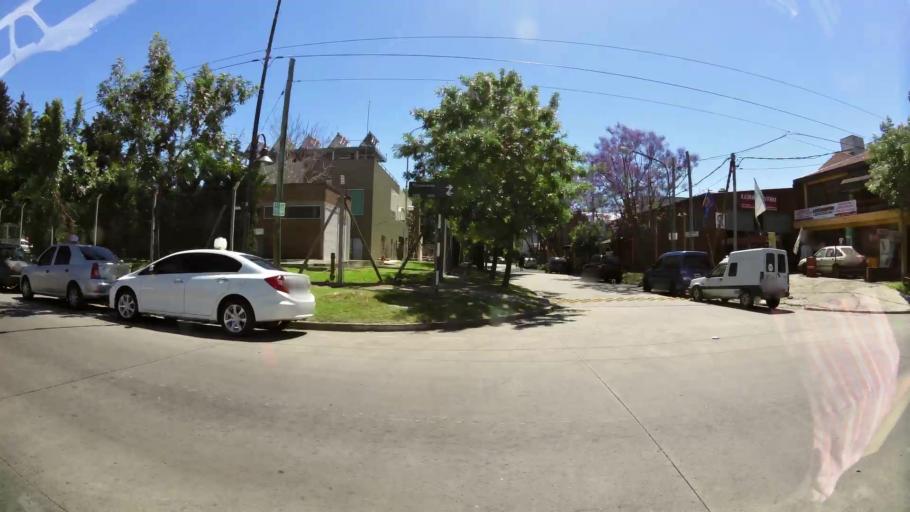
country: AR
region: Buenos Aires
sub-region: Partido de General San Martin
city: General San Martin
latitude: -34.5358
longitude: -58.5473
